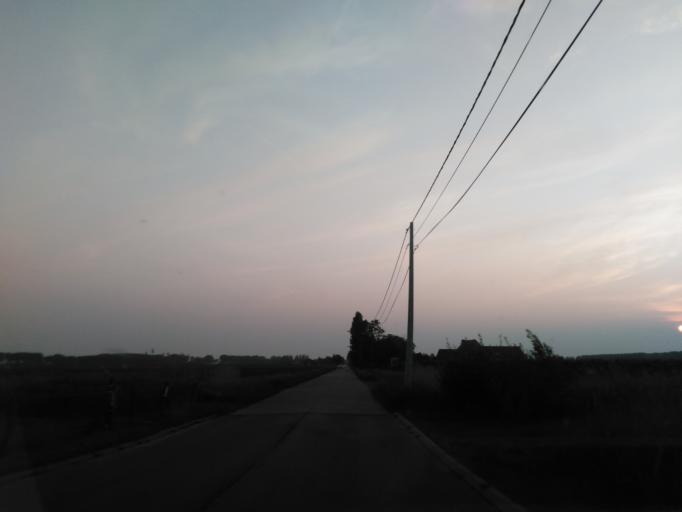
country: BE
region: Flanders
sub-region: Provincie Oost-Vlaanderen
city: Beveren
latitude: 51.2885
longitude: 4.2025
